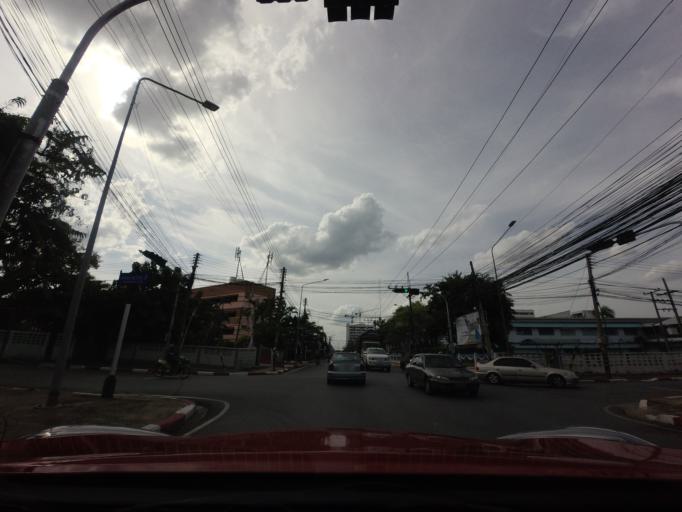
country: TH
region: Yala
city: Yala
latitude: 6.5439
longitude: 101.2783
